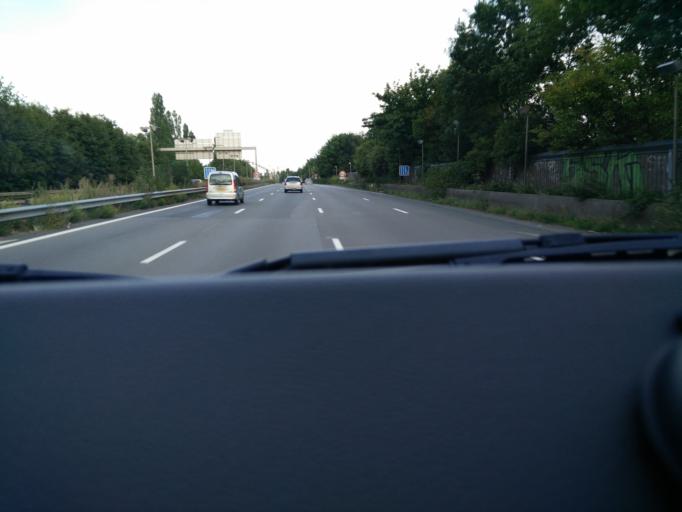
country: FR
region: Nord-Pas-de-Calais
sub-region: Departement du Nord
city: Hallennes-lez-Haubourdin
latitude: 50.6196
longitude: 2.9746
